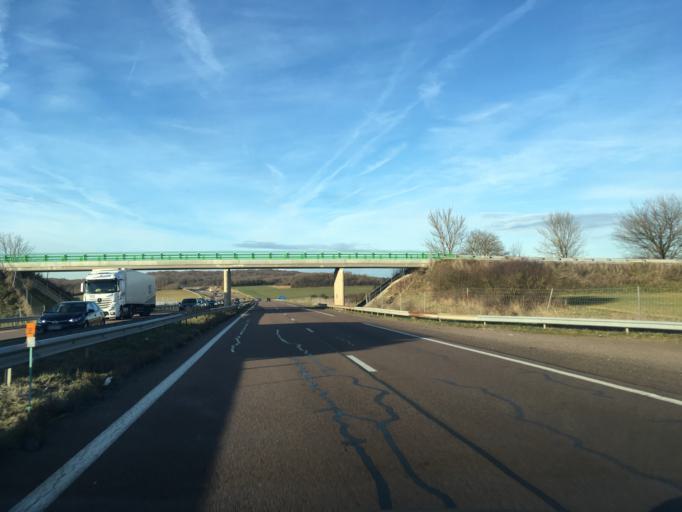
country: FR
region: Bourgogne
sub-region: Departement de l'Yonne
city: Joux-la-Ville
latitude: 47.5706
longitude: 3.9384
